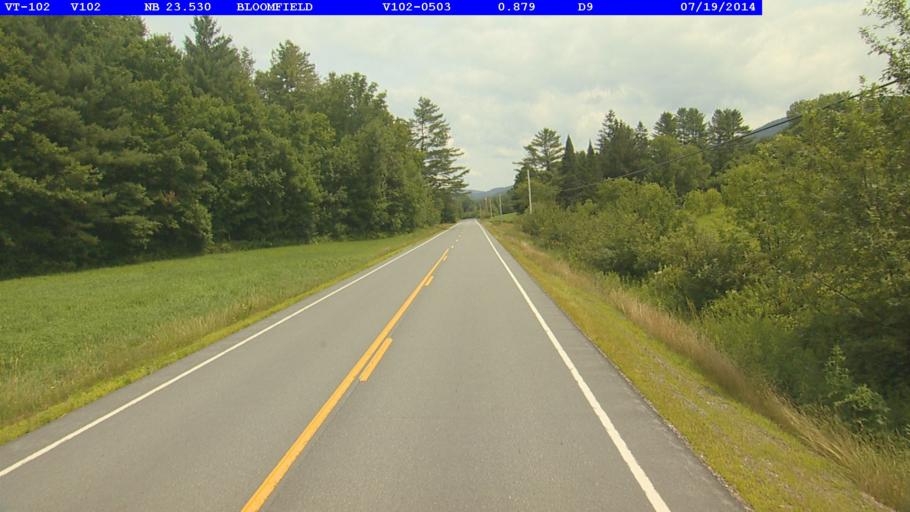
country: US
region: New Hampshire
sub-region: Coos County
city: Stratford
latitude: 44.7573
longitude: -71.6223
